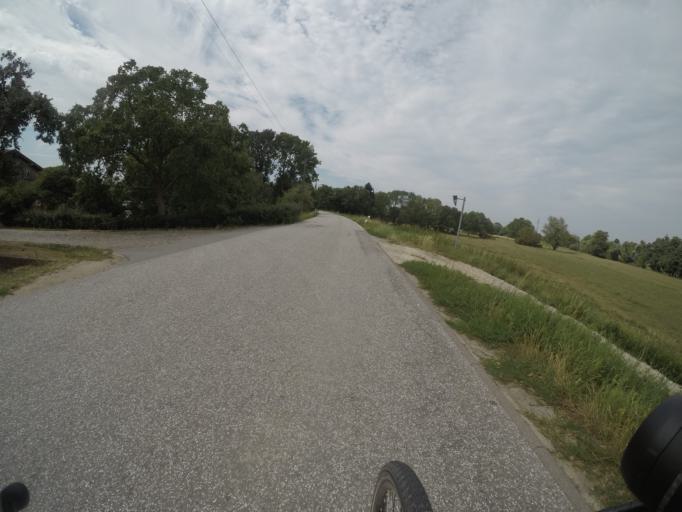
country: DE
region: Schleswig-Holstein
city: Oststeinbek
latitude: 53.4758
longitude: 10.1357
